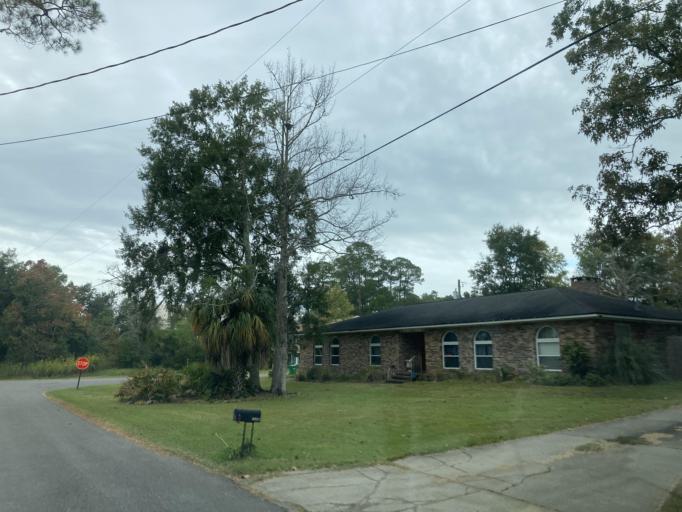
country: US
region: Mississippi
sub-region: Jackson County
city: Gulf Hills
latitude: 30.4321
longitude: -88.8437
